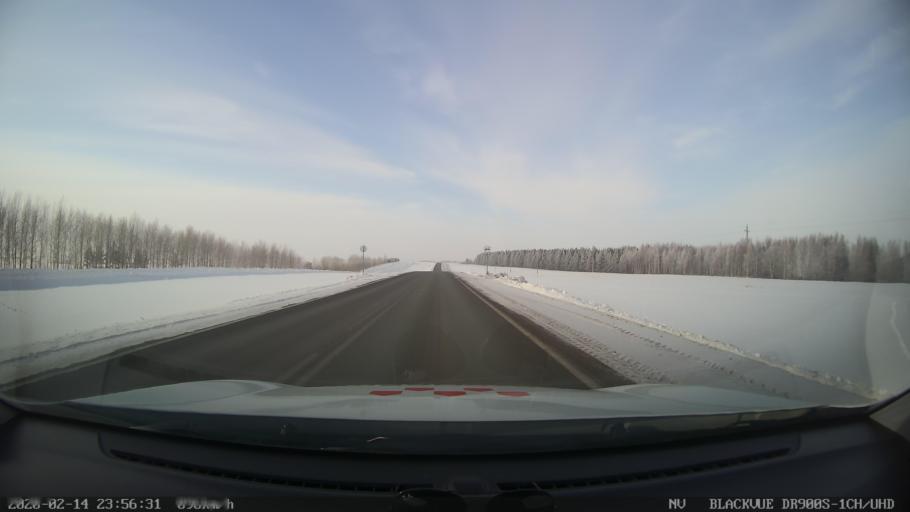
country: RU
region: Tatarstan
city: Kuybyshevskiy Zaton
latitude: 55.3254
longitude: 49.1287
